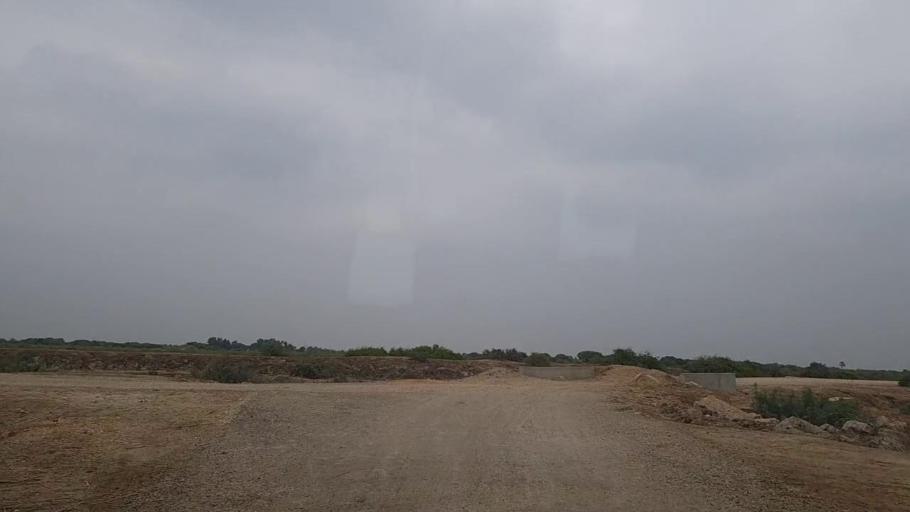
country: PK
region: Sindh
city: Mirpur Sakro
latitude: 24.6345
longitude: 67.7201
